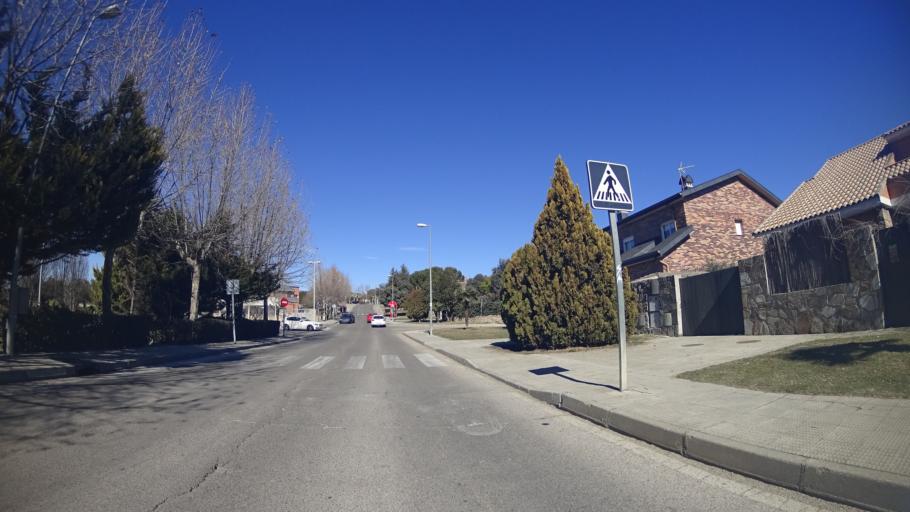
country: ES
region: Madrid
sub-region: Provincia de Madrid
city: Colmenarejo
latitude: 40.5548
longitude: -4.0131
